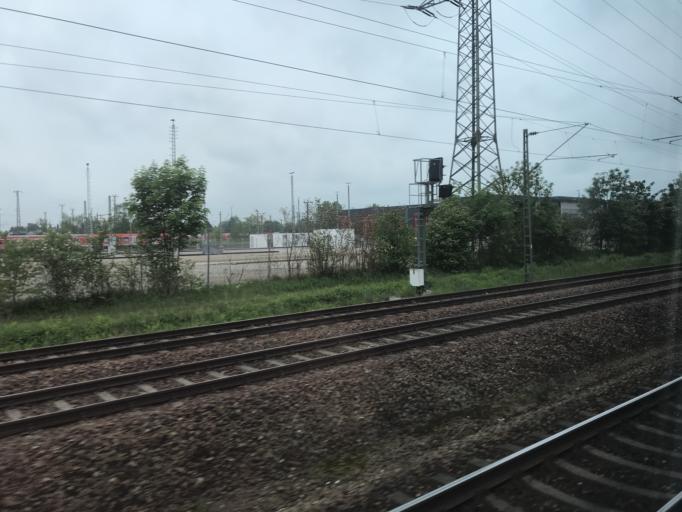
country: DE
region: Bavaria
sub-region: Upper Bavaria
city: Pasing
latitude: 48.1595
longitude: 11.4392
